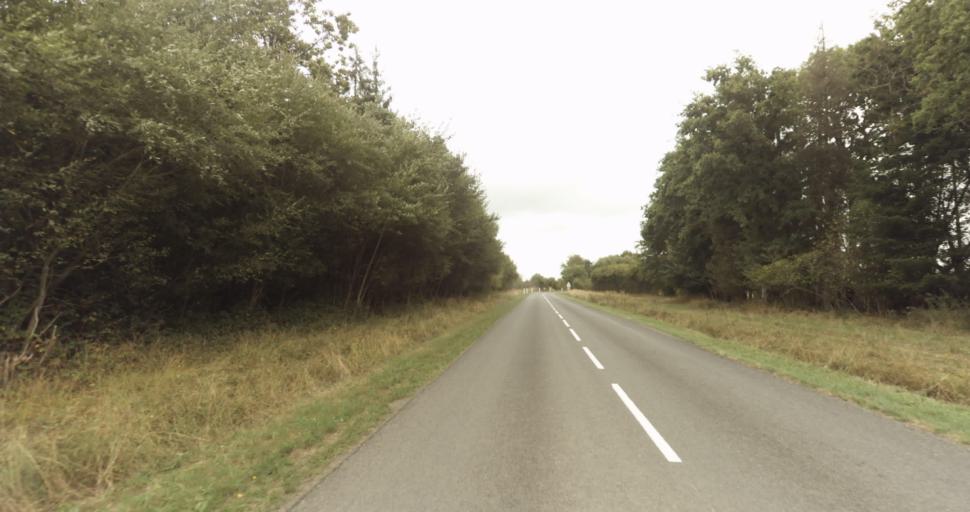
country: FR
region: Lower Normandy
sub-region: Departement de l'Orne
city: Gace
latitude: 48.8015
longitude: 0.3440
